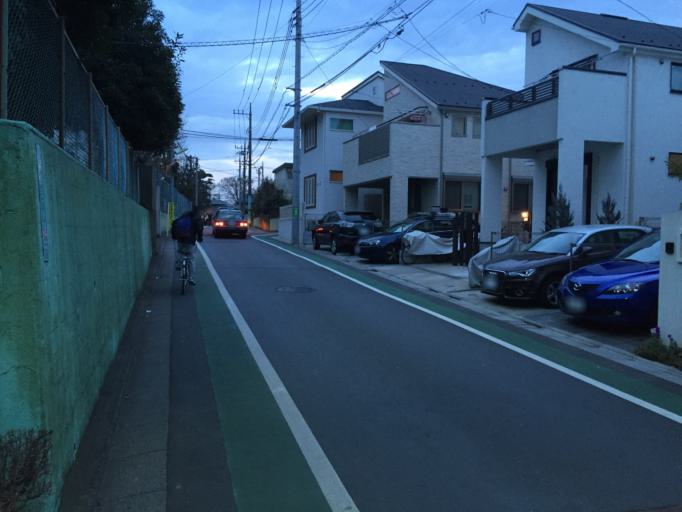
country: JP
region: Tokyo
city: Tokyo
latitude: 35.6620
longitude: 139.6318
